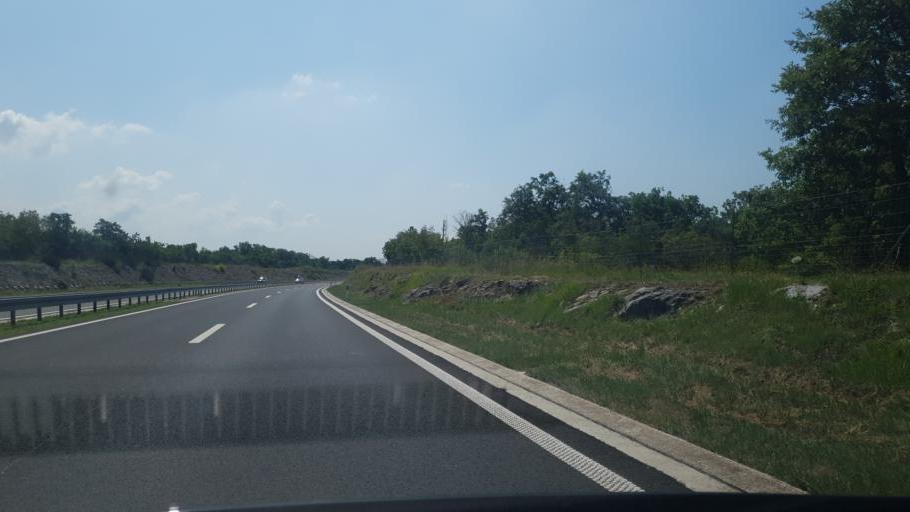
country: HR
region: Istarska
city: Vodnjan
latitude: 45.0262
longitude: 13.8386
